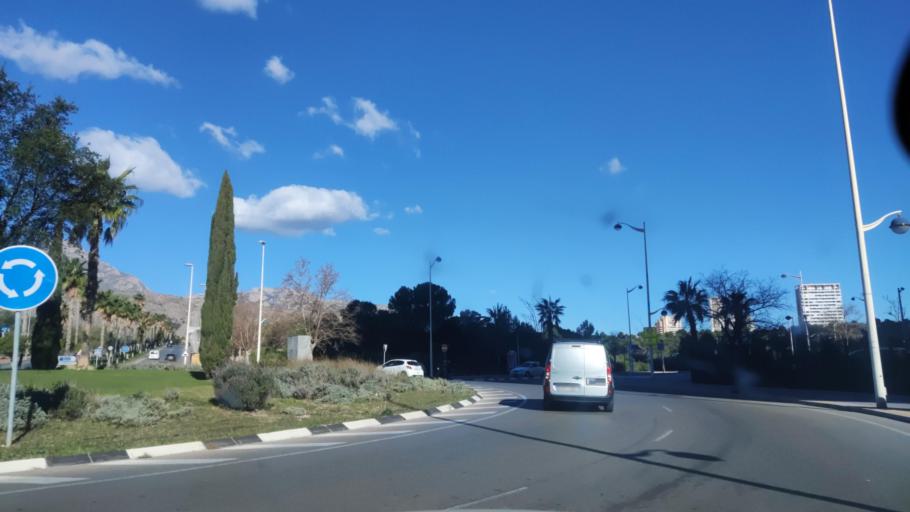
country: ES
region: Valencia
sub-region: Provincia de Alicante
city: Benidorm
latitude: 38.5374
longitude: -0.1581
